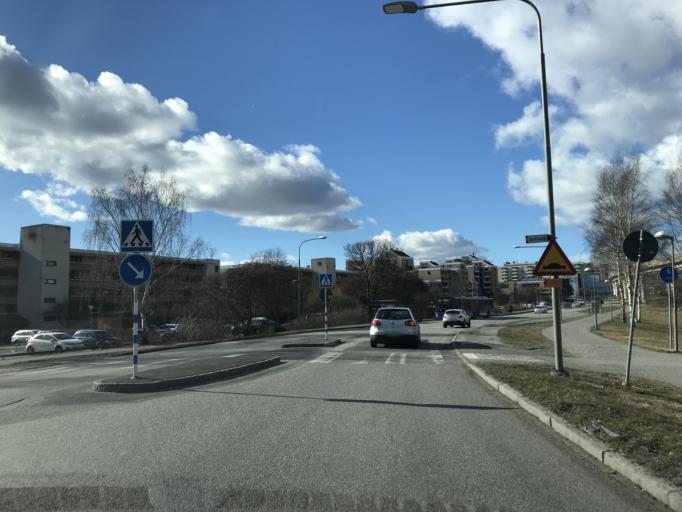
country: SE
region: Stockholm
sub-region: Stockholms Kommun
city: Kista
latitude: 59.3991
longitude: 17.9481
